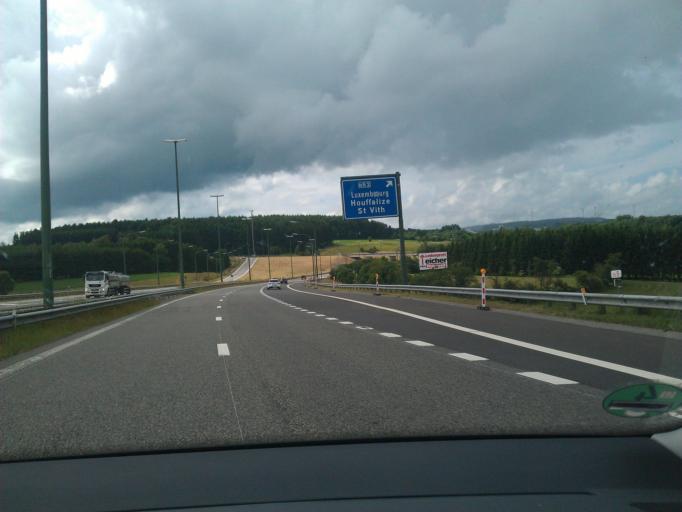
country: BE
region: Wallonia
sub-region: Province de Liege
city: Saint-Vith
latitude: 50.2632
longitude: 6.1217
